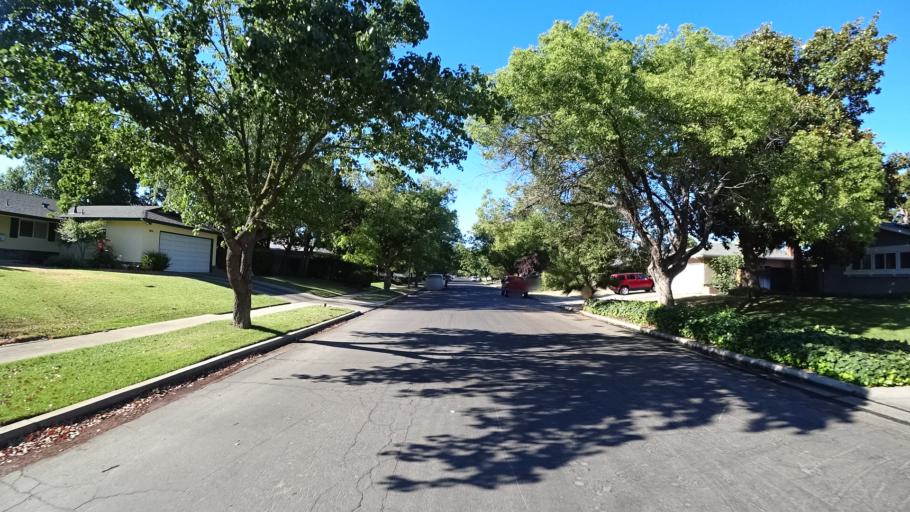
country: US
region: California
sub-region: Fresno County
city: Fresno
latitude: 36.8062
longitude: -119.8304
